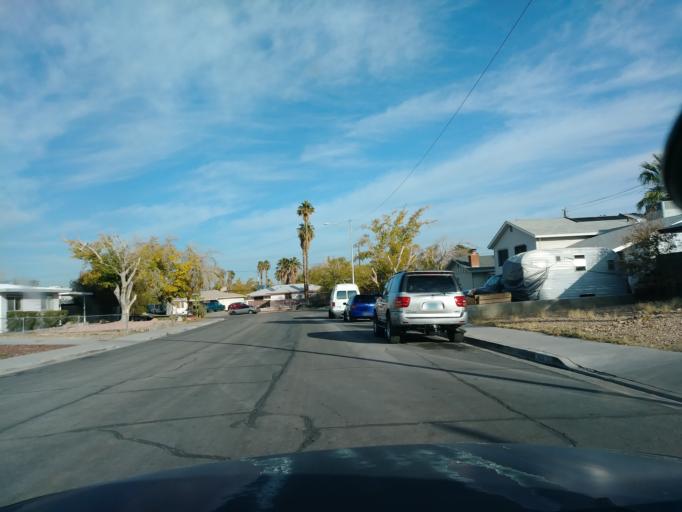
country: US
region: Nevada
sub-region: Clark County
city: Spring Valley
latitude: 36.1674
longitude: -115.2271
